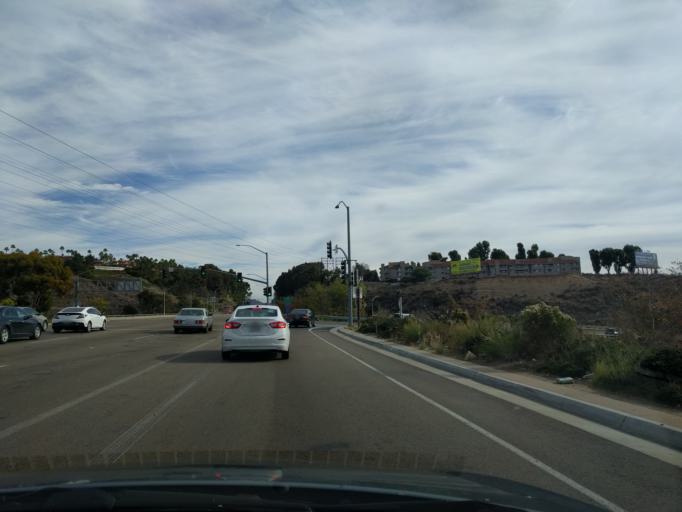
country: US
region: California
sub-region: San Diego County
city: San Diego
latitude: 32.7877
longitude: -117.1158
